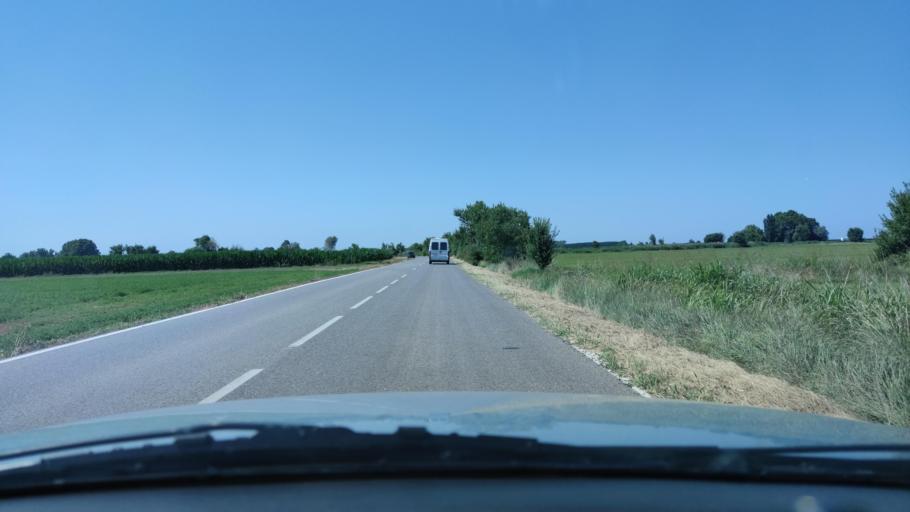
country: ES
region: Catalonia
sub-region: Provincia de Lleida
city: Castellsera
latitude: 41.7342
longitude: 0.9838
